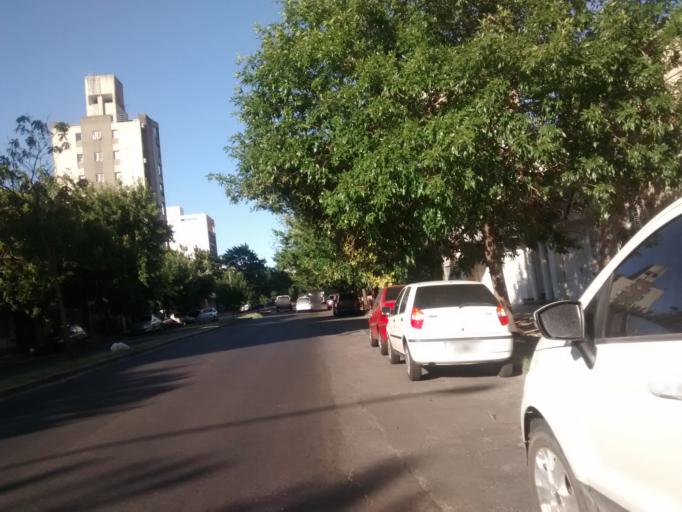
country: AR
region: Buenos Aires
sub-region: Partido de La Plata
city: La Plata
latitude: -34.9301
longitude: -57.9516
